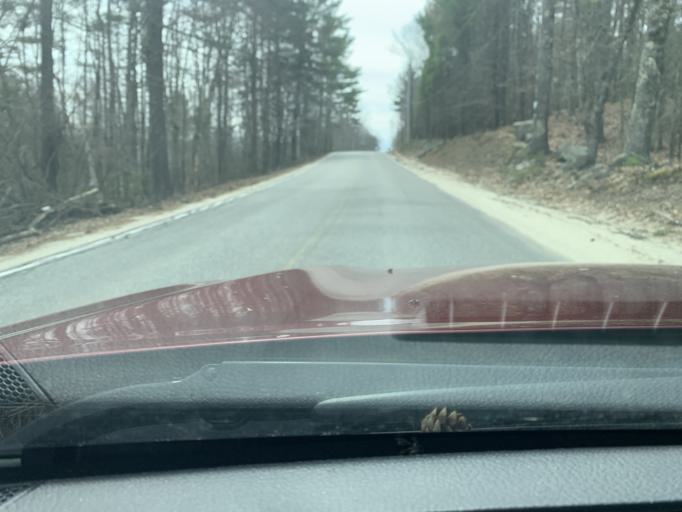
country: US
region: Maine
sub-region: Cumberland County
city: Raymond
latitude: 43.9465
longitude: -70.3862
